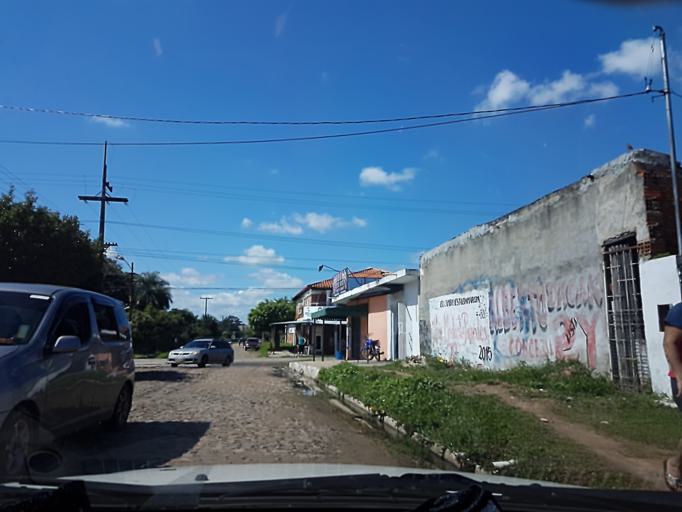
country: PY
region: Central
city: Colonia Mariano Roque Alonso
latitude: -25.2085
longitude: -57.5337
